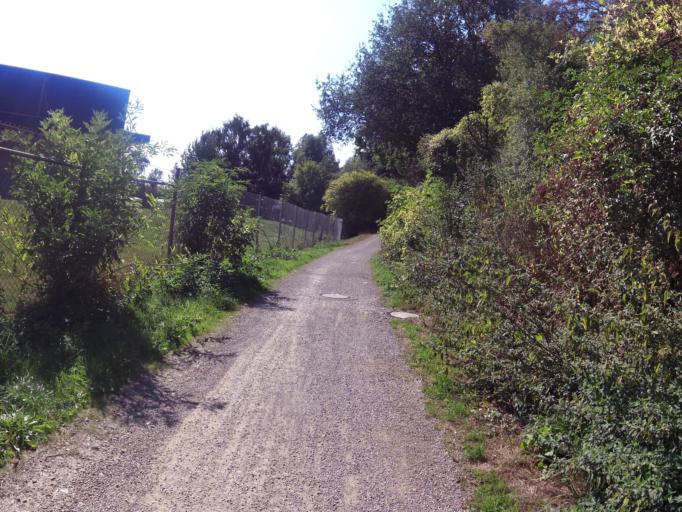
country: DE
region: North Rhine-Westphalia
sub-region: Regierungsbezirk Koln
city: Wurselen
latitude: 50.7994
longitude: 6.1164
